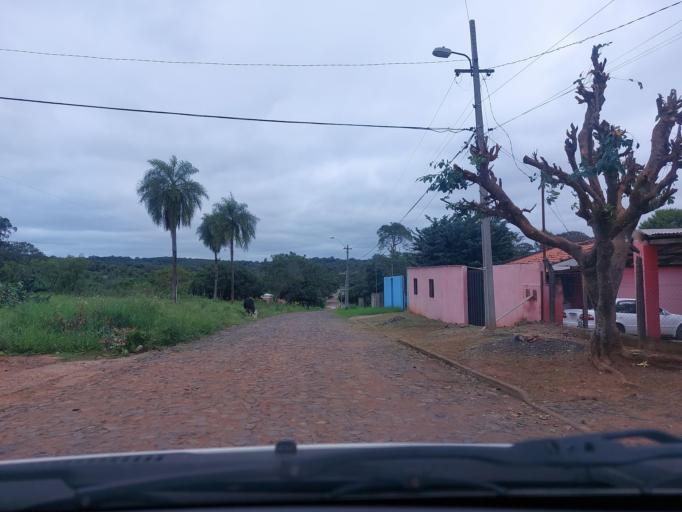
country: PY
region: San Pedro
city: Guayaybi
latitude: -24.6654
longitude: -56.4315
